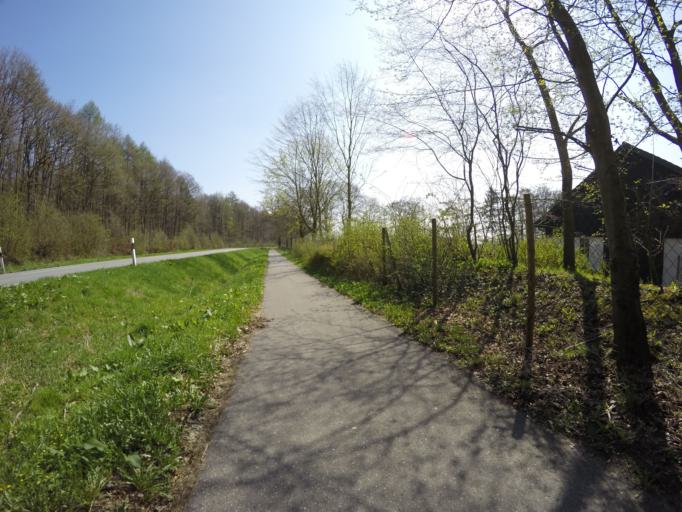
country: DE
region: Schleswig-Holstein
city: Bilsen
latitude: 53.7499
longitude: 9.8776
